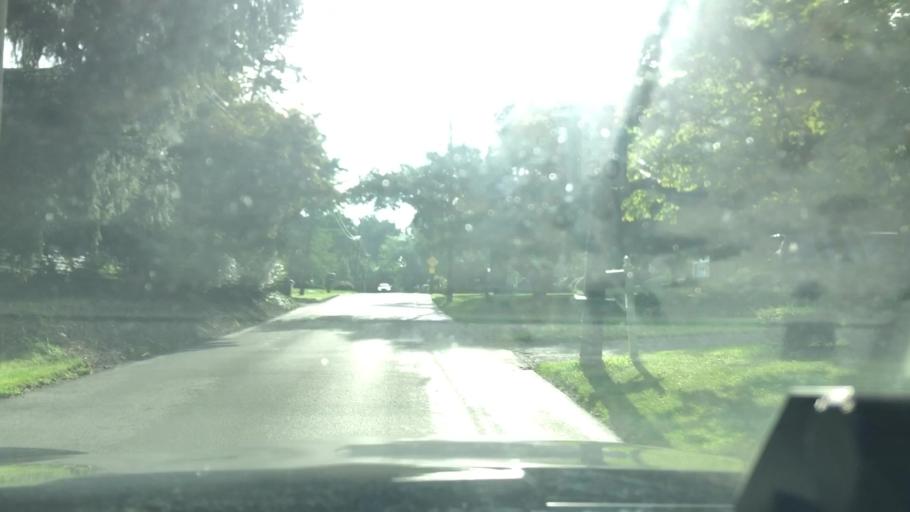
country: US
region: Pennsylvania
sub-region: Northampton County
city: Bethlehem
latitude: 40.6551
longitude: -75.3712
